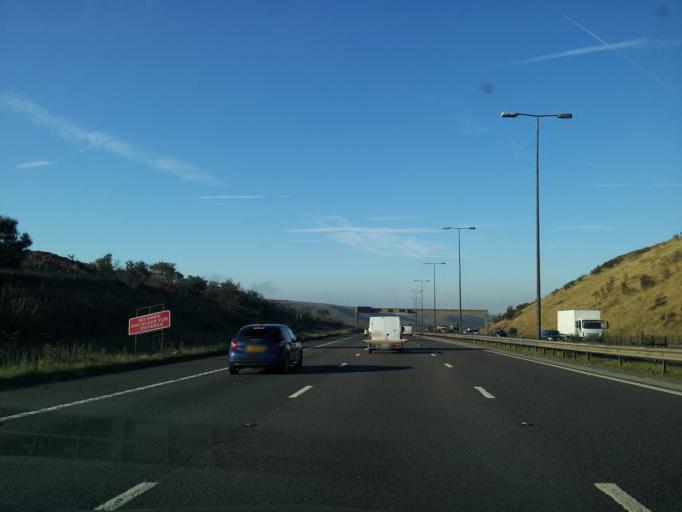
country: GB
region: England
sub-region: Borough of Rochdale
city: Littleborough
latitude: 53.6276
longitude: -2.0414
